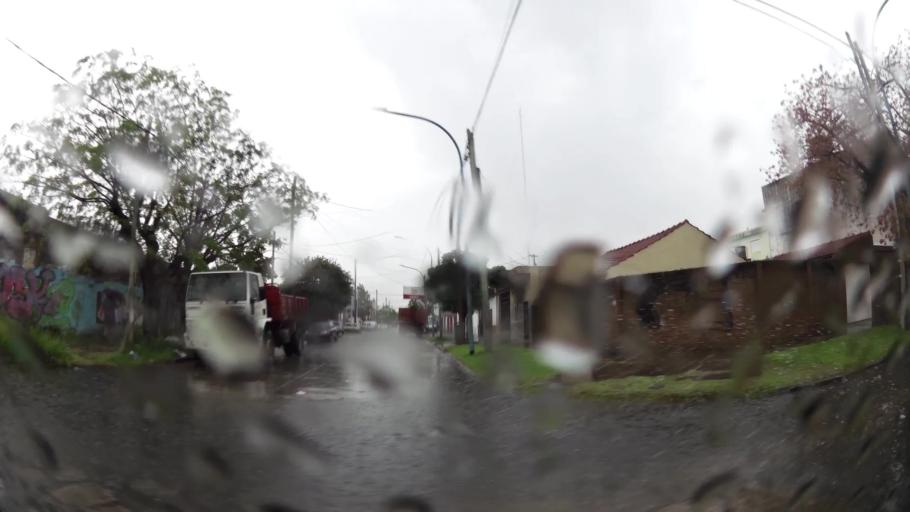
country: AR
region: Buenos Aires
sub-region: Partido de Lanus
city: Lanus
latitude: -34.7093
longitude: -58.4091
